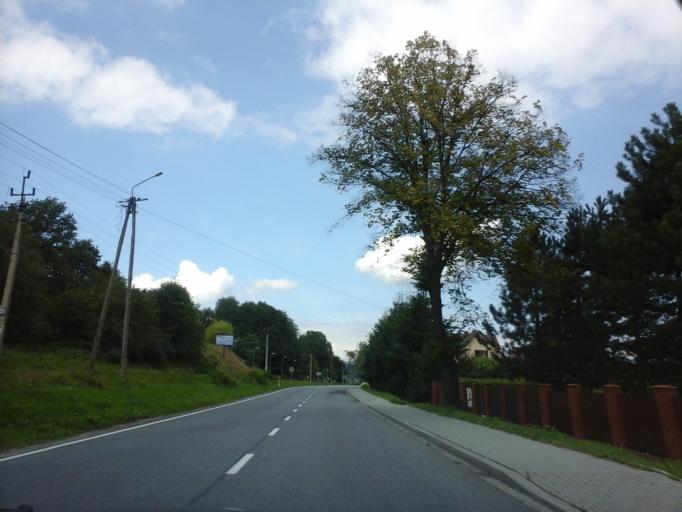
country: PL
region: Lesser Poland Voivodeship
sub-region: Powiat suski
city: Juszczyn
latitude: 49.7055
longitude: 19.6939
